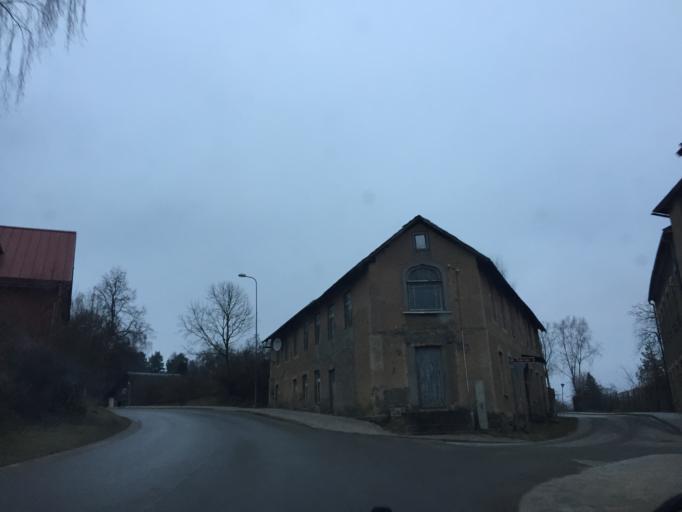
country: LV
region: Raunas
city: Rauna
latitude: 57.3337
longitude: 25.6086
